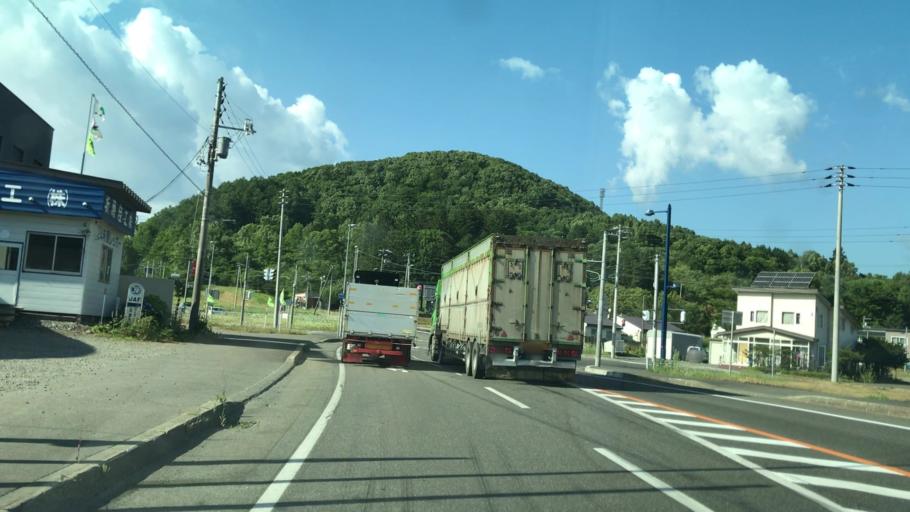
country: JP
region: Hokkaido
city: Shimo-furano
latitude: 42.8811
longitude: 142.4349
